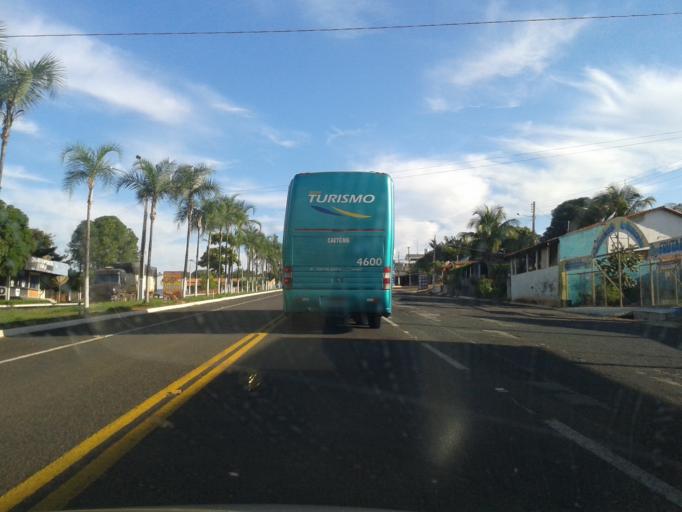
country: BR
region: Minas Gerais
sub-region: Tupaciguara
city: Tupaciguara
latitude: -18.3150
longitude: -48.5624
